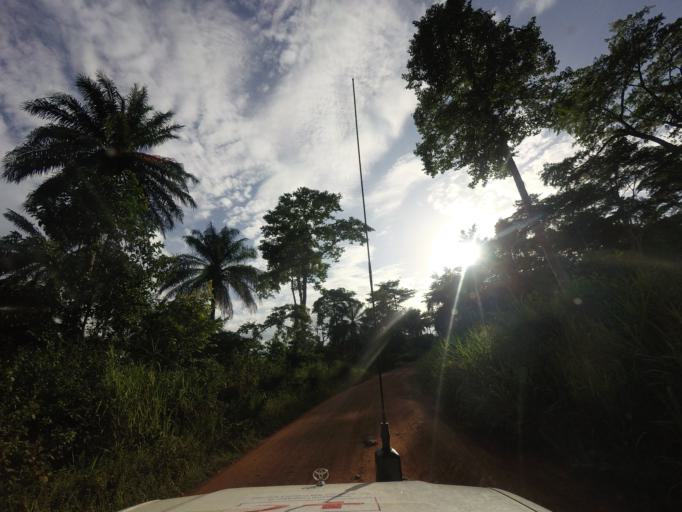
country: GN
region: Nzerekore
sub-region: Nzerekore Prefecture
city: Nzerekore
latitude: 7.6608
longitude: -8.8012
